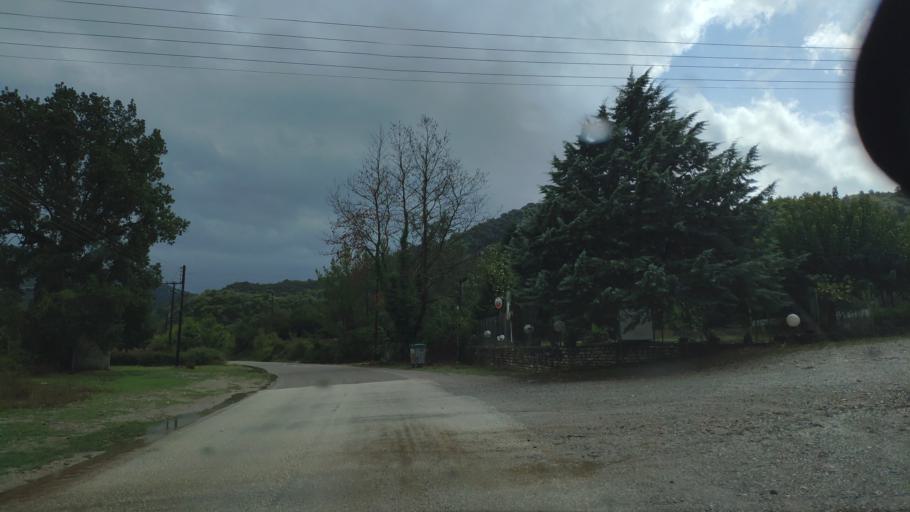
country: GR
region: West Greece
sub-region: Nomos Aitolias kai Akarnanias
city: Krikellos
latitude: 38.9638
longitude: 21.3288
